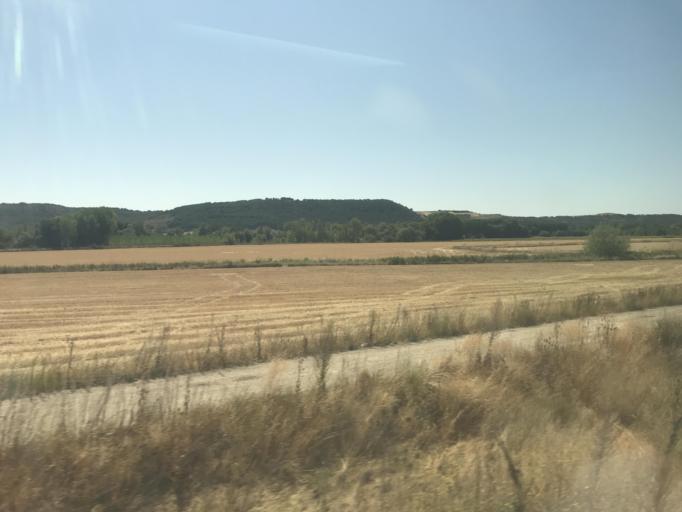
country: ES
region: Castille and Leon
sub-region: Provincia de Burgos
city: Villaldemiro
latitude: 42.2390
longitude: -3.9738
